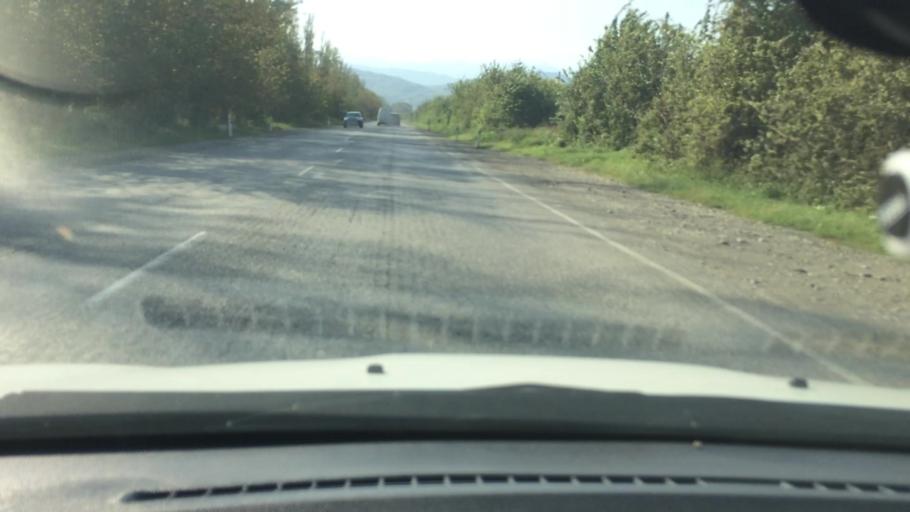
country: GE
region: Imereti
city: Samtredia
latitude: 42.1428
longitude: 42.3349
